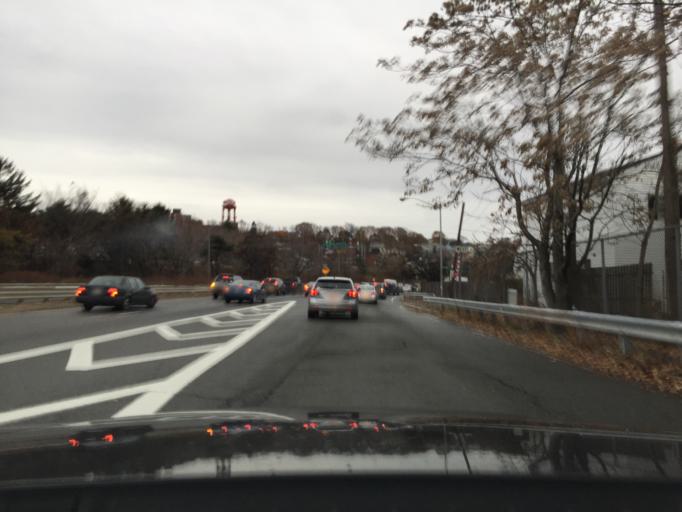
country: US
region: Massachusetts
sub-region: Suffolk County
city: Chelsea
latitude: 42.4059
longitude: -71.0277
